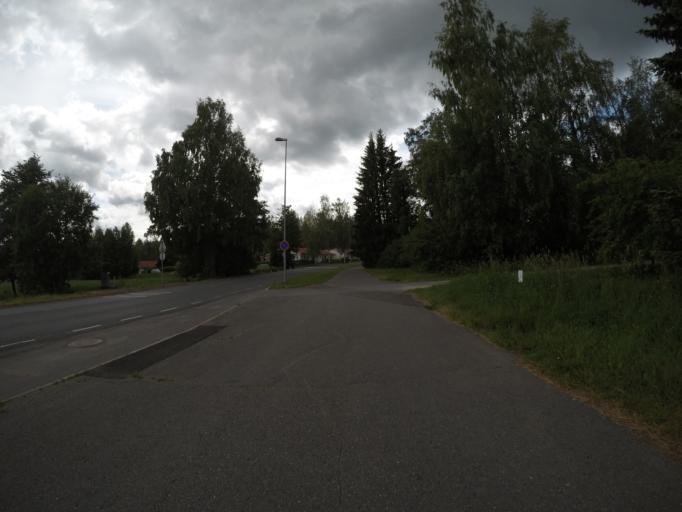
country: FI
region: Haeme
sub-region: Haemeenlinna
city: Haemeenlinna
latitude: 60.9764
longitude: 24.4344
